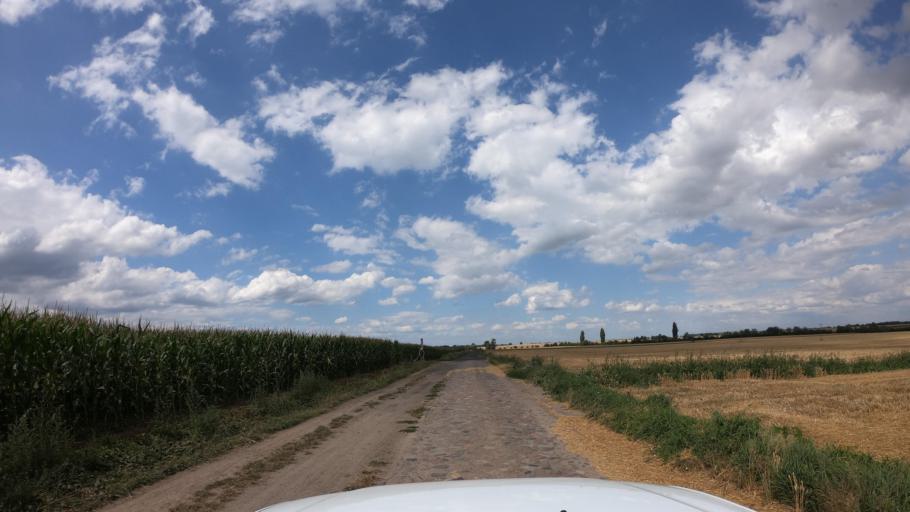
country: PL
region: West Pomeranian Voivodeship
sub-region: Powiat pyrzycki
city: Warnice
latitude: 53.2446
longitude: 14.9128
